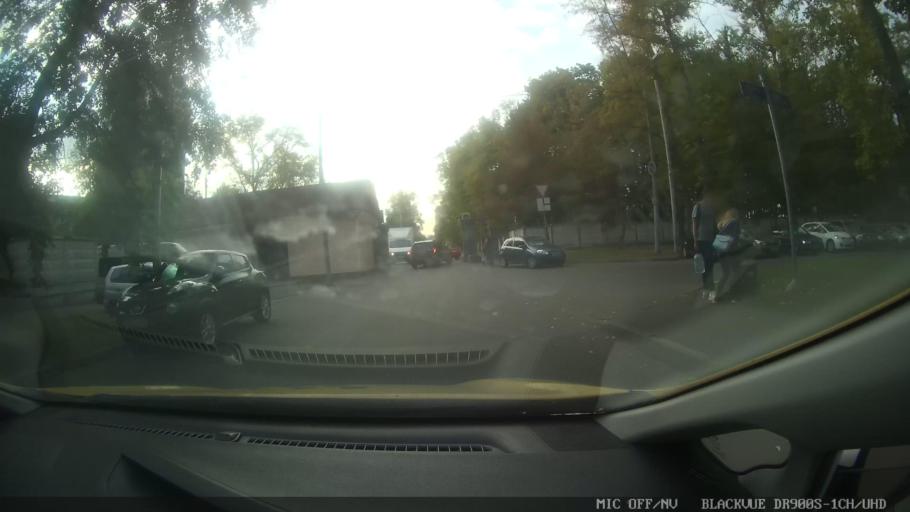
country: RU
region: Moscow
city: Vatutino
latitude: 55.8588
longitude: 37.6963
